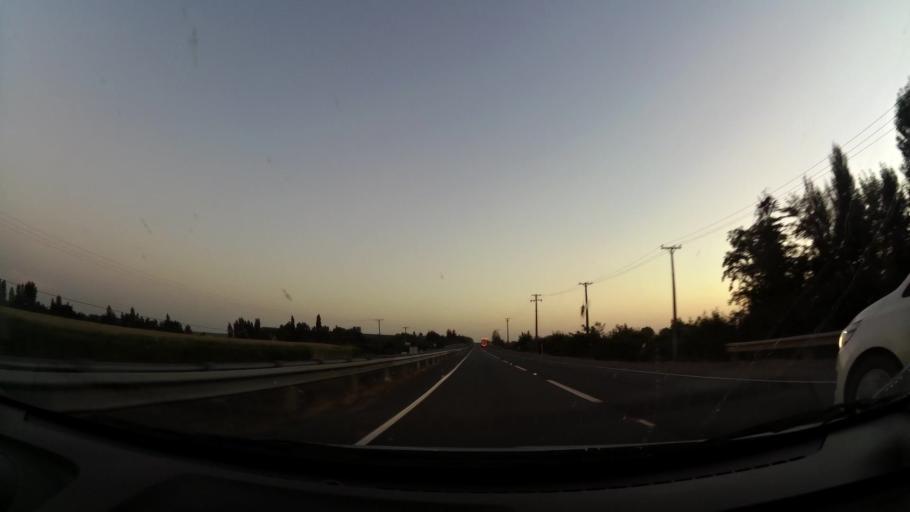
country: CL
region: Maule
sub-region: Provincia de Linares
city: Parral
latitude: -36.0754
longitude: -71.7886
